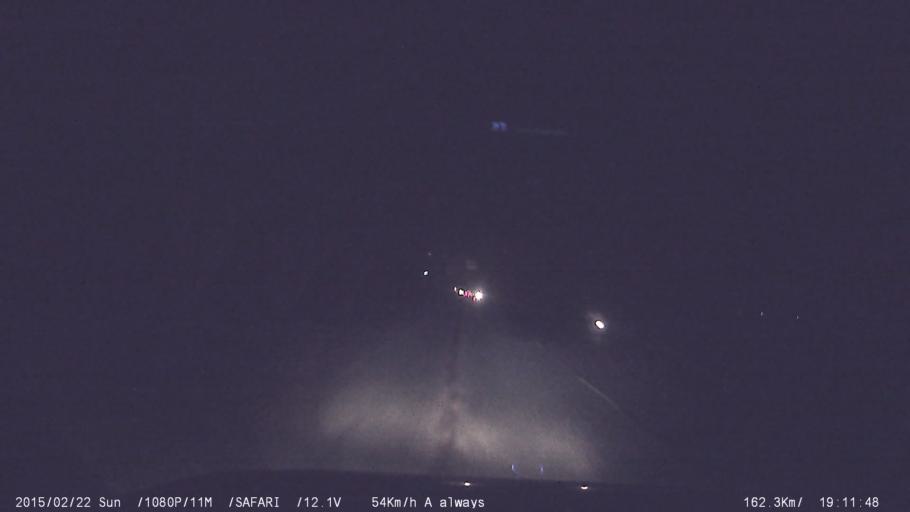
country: IN
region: Tamil Nadu
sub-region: Theni
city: Periyakulam
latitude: 10.0692
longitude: 77.5150
